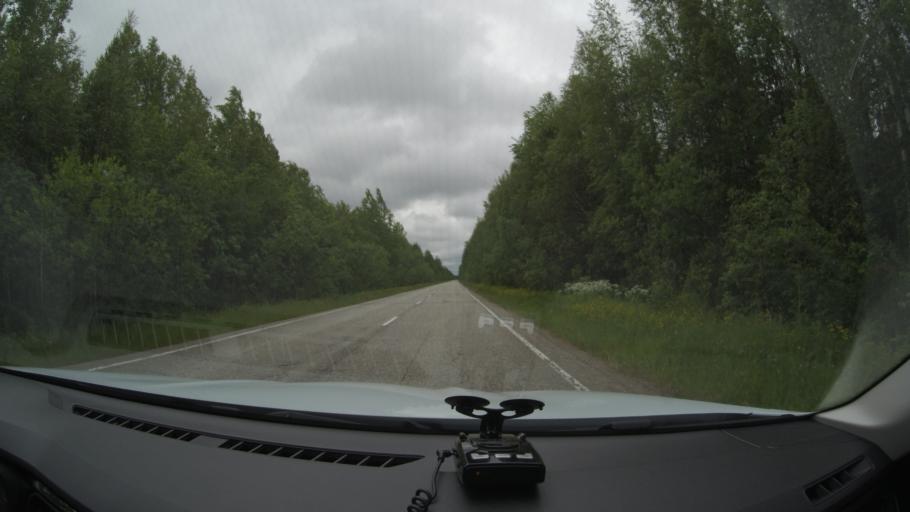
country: RU
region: Komi Republic
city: Nizhniy Odes
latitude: 63.6285
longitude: 54.6265
